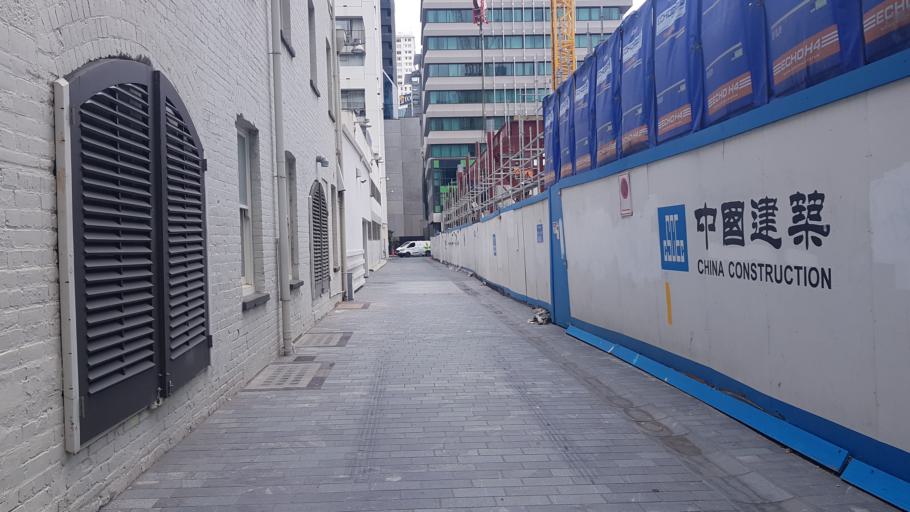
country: NZ
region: Auckland
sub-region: Auckland
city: Auckland
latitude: -36.8459
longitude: 174.7699
